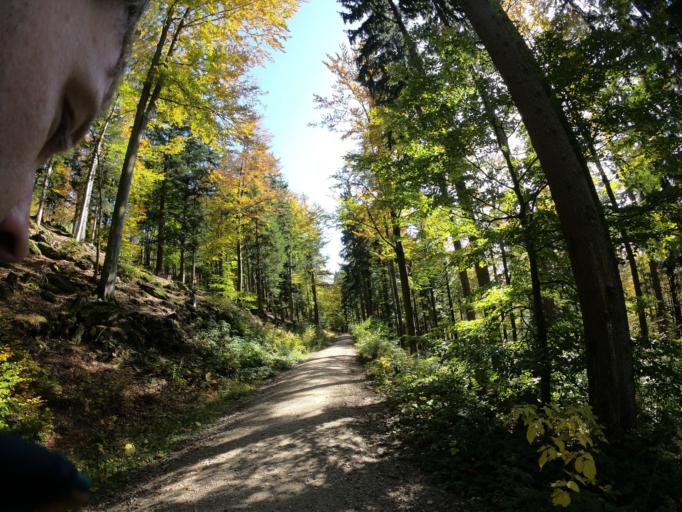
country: DE
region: Bavaria
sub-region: Lower Bavaria
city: Bodenmais
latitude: 49.0818
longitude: 13.1176
